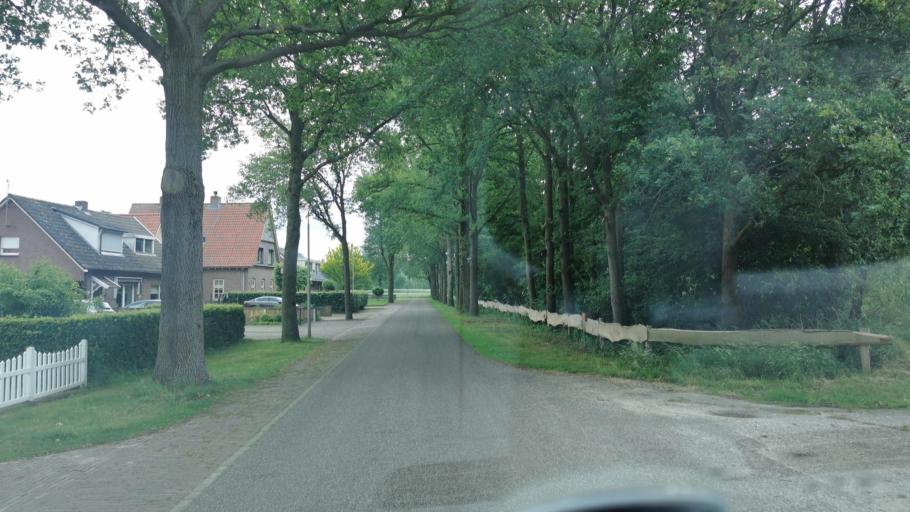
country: DE
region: North Rhine-Westphalia
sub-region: Regierungsbezirk Munster
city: Gronau
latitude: 52.2286
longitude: 7.0268
